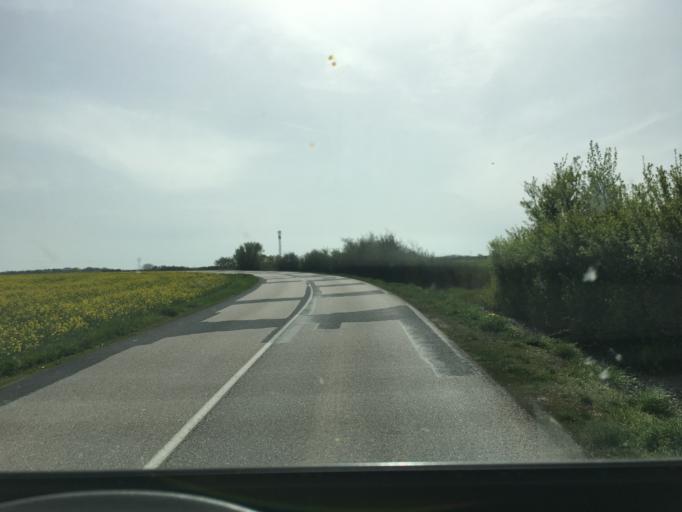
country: FR
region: Lorraine
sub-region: Departement de Meurthe-et-Moselle
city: Art-sur-Meurthe
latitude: 48.6156
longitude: 6.2591
